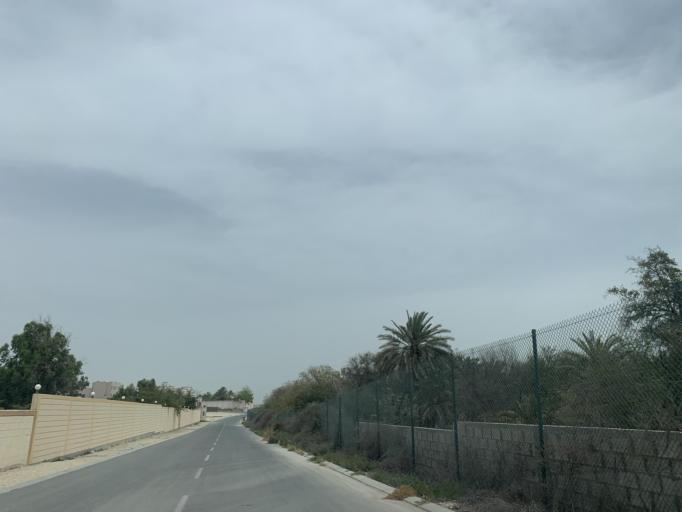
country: BH
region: Northern
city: Ar Rifa'
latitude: 26.1384
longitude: 50.5413
